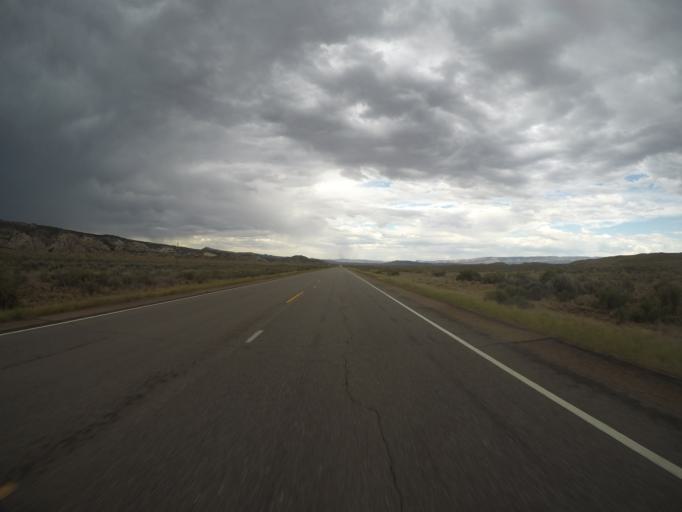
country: US
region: Colorado
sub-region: Rio Blanco County
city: Rangely
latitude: 40.2507
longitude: -108.7830
